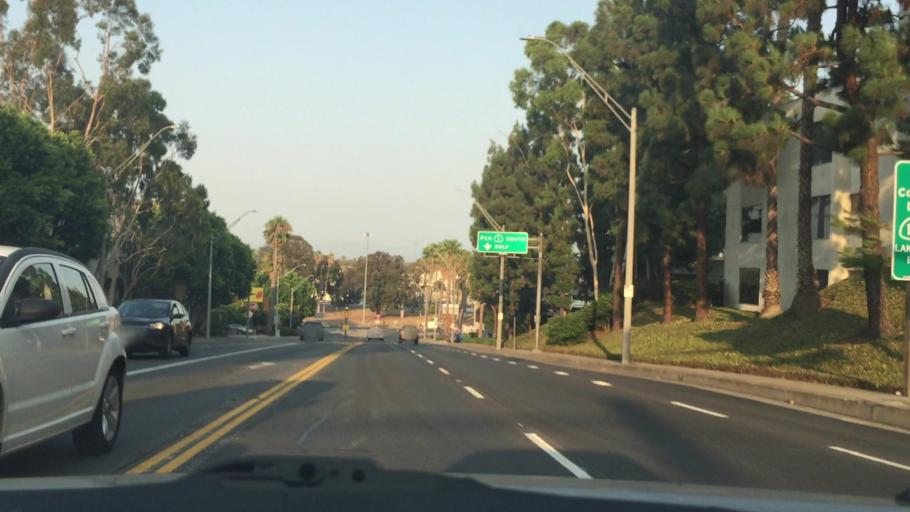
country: US
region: California
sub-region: Los Angeles County
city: Signal Hill
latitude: 33.7899
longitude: -118.1457
